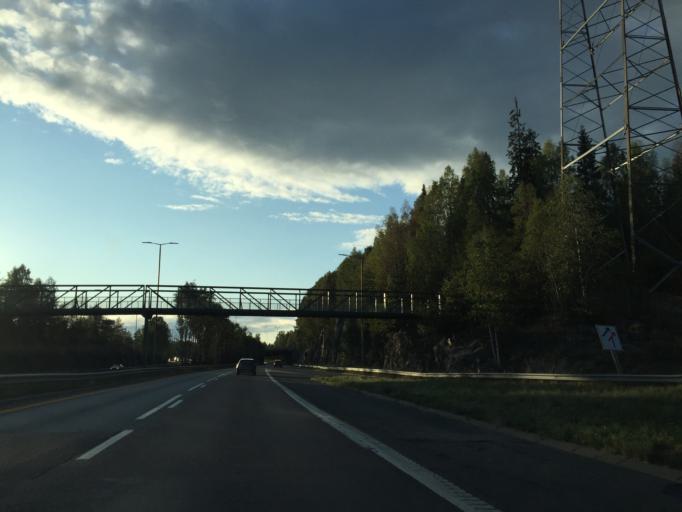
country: NO
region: Akershus
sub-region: Lorenskog
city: Kjenn
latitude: 59.9374
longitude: 10.9339
